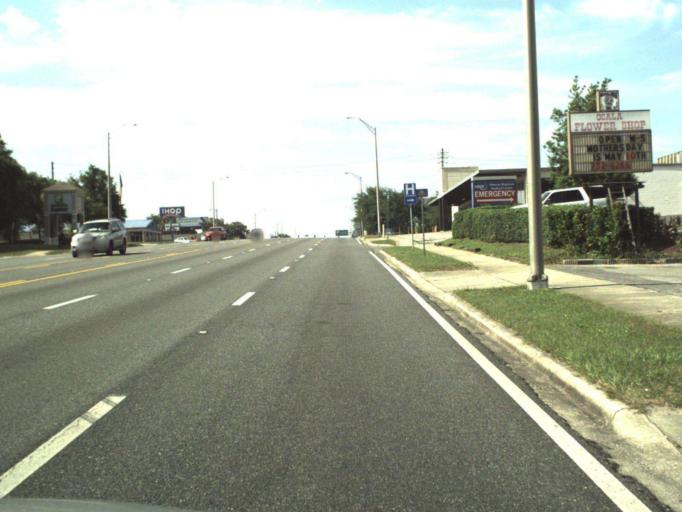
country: US
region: Florida
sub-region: Marion County
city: Ocala
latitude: 29.1754
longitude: -82.1404
